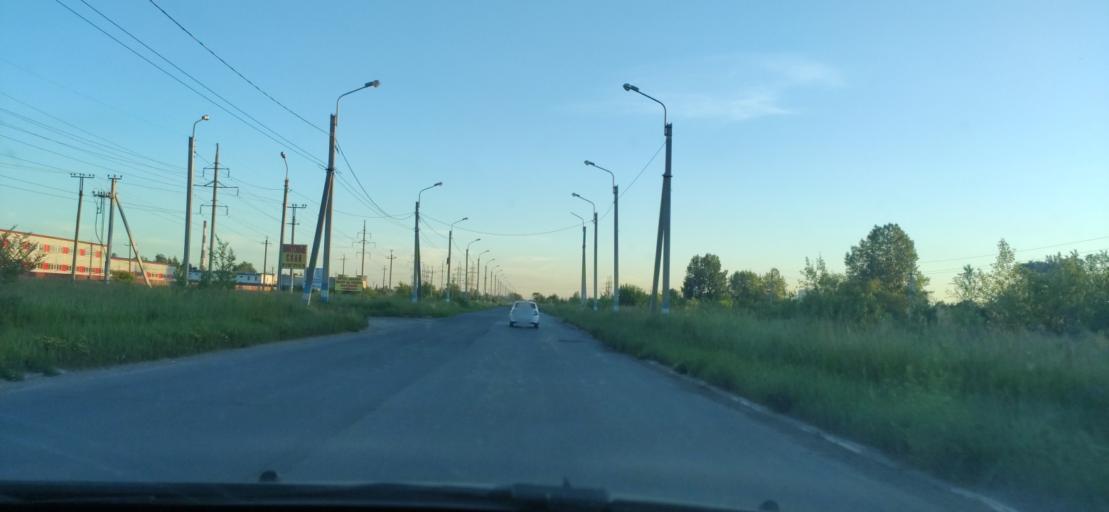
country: RU
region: Ulyanovsk
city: Mirnyy
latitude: 54.3726
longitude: 48.6488
